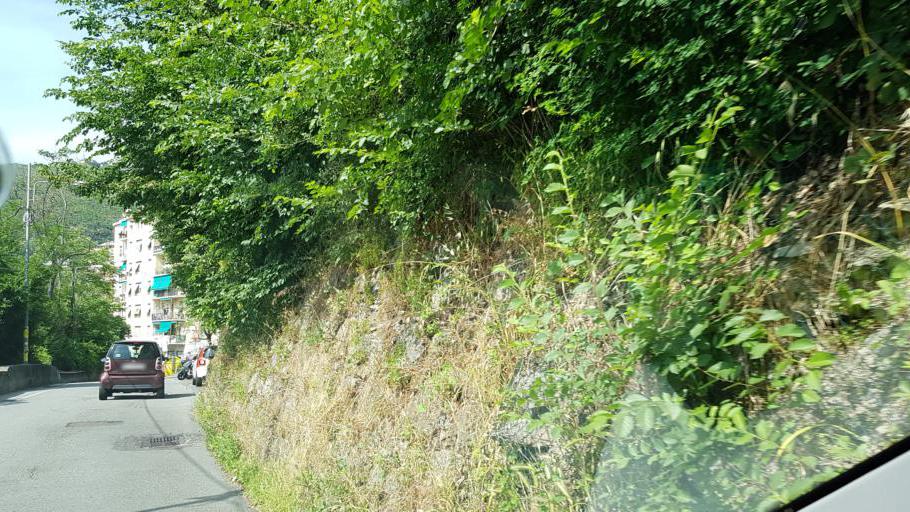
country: IT
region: Liguria
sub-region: Provincia di Genova
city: Genoa
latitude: 44.4060
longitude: 8.9890
